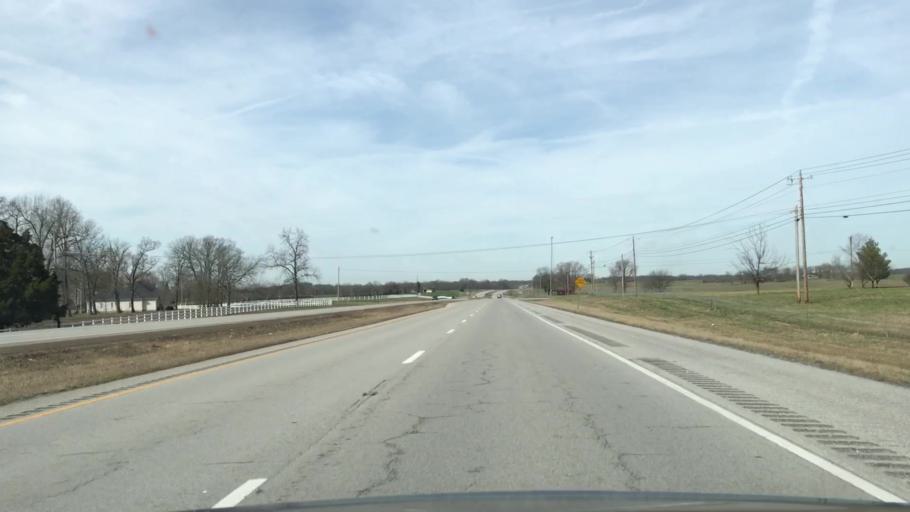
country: US
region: Kentucky
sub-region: Christian County
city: Hopkinsville
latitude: 36.8794
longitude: -87.5777
